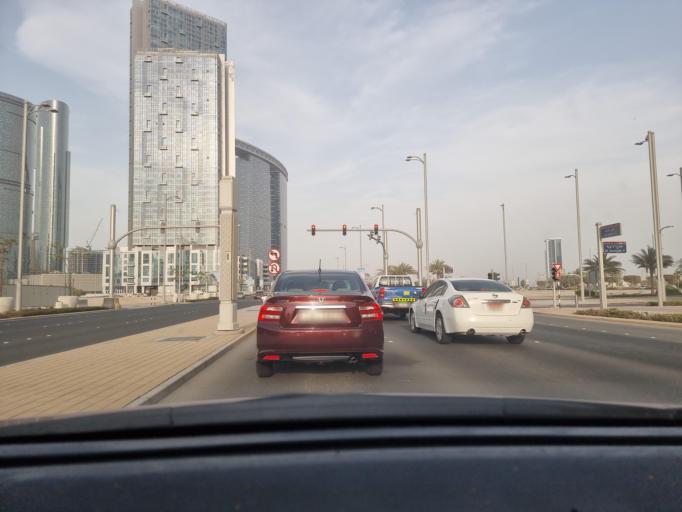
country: AE
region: Abu Dhabi
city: Abu Dhabi
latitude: 24.4936
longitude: 54.4006
